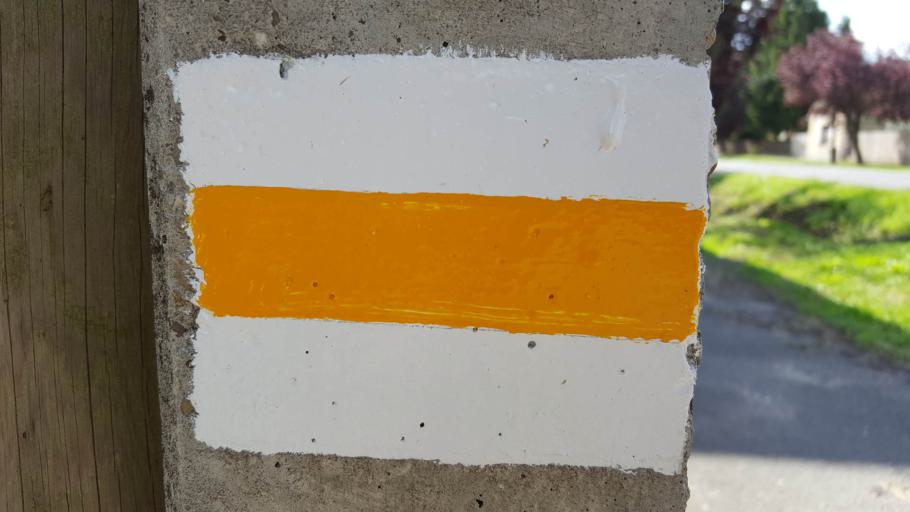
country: HU
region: Somogy
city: Marcali
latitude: 46.5047
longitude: 17.4242
